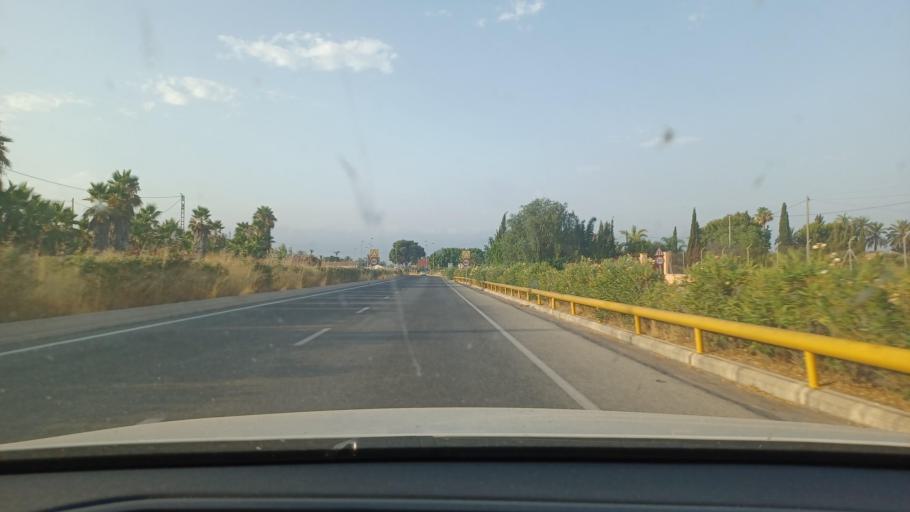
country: ES
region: Valencia
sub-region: Provincia de Alicante
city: Elche
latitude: 38.2177
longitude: -0.6973
